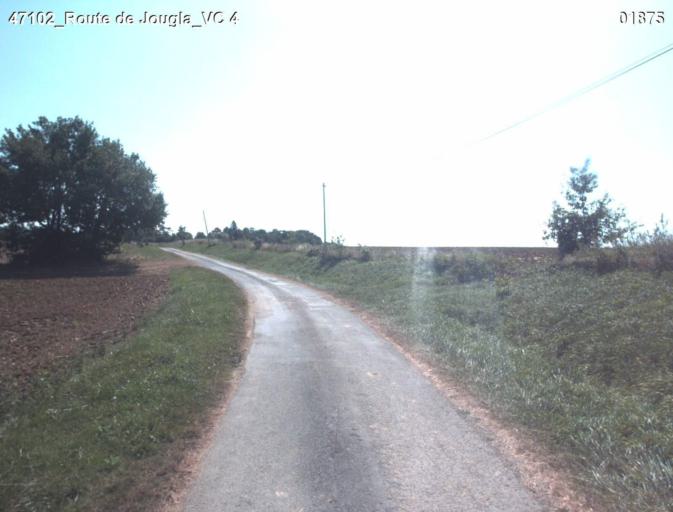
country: FR
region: Aquitaine
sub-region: Departement du Lot-et-Garonne
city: Laplume
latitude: 44.0576
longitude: 0.4328
